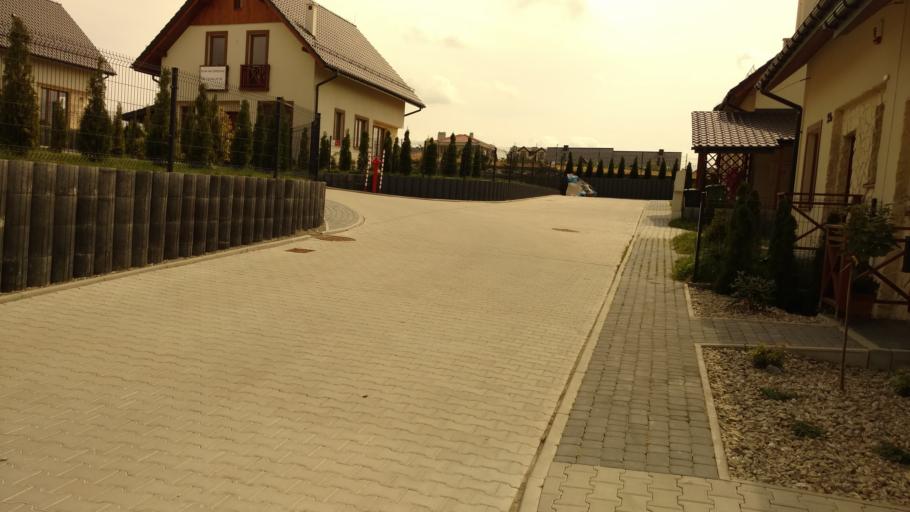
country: PL
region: Lesser Poland Voivodeship
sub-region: Powiat krakowski
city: Michalowice
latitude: 50.1312
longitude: 19.9571
